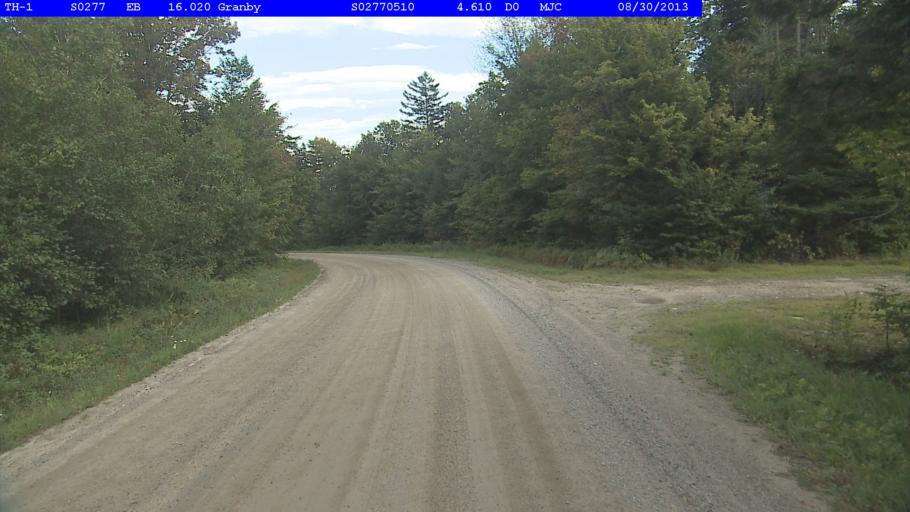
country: US
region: Vermont
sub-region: Essex County
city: Guildhall
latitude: 44.5780
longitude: -71.6812
